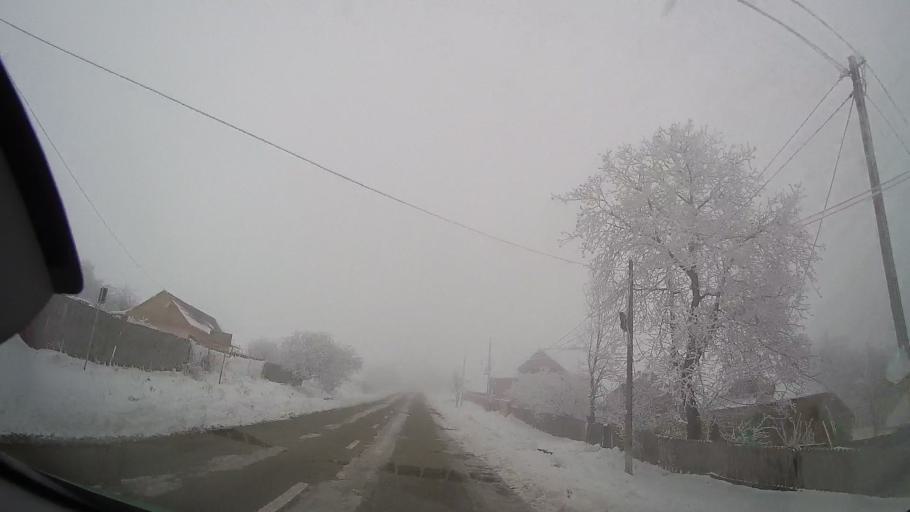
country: RO
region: Neamt
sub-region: Comuna Valea Ursului
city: Valea Ursului
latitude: 46.8007
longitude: 27.0754
